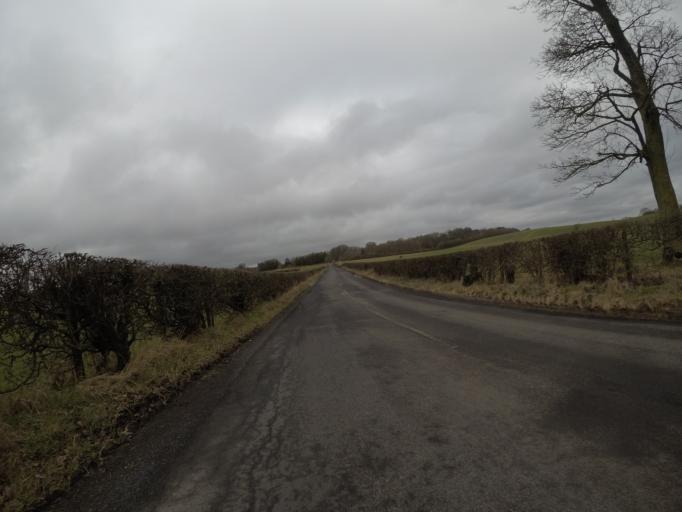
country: GB
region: Scotland
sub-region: North Ayrshire
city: Springside
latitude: 55.6244
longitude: -4.6117
